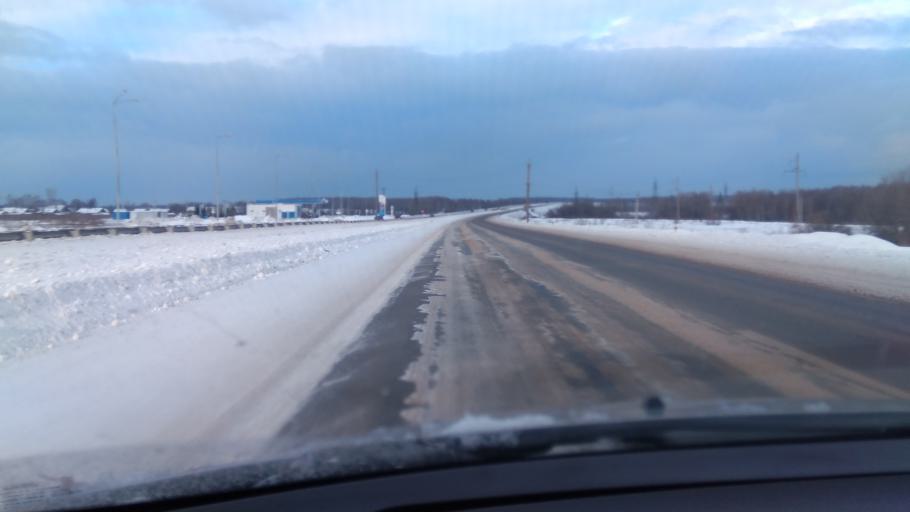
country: RU
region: Sverdlovsk
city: Tsementnyy
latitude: 57.4955
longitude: 60.1757
